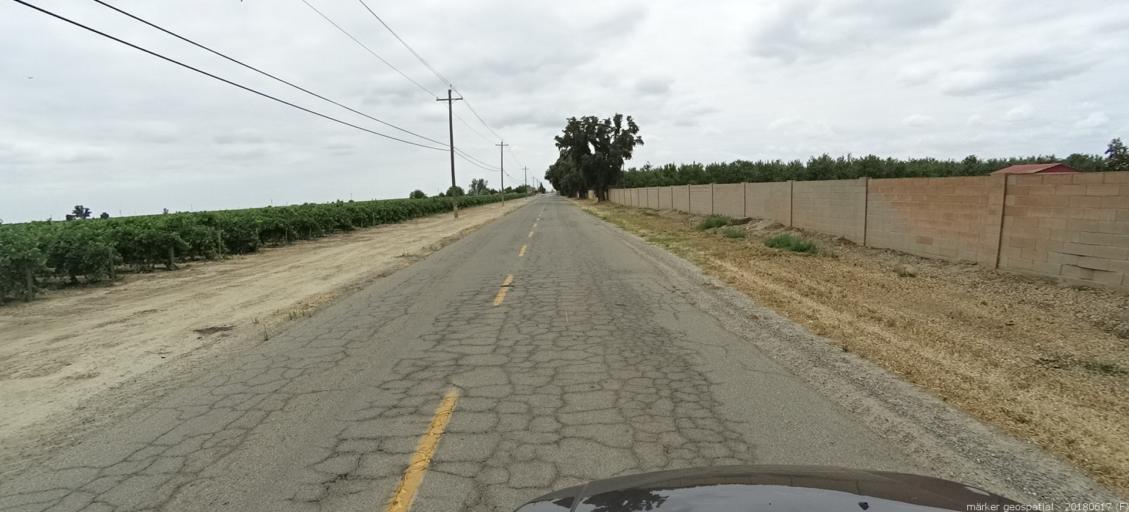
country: US
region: California
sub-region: Madera County
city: Madera
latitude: 36.9003
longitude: -120.1652
